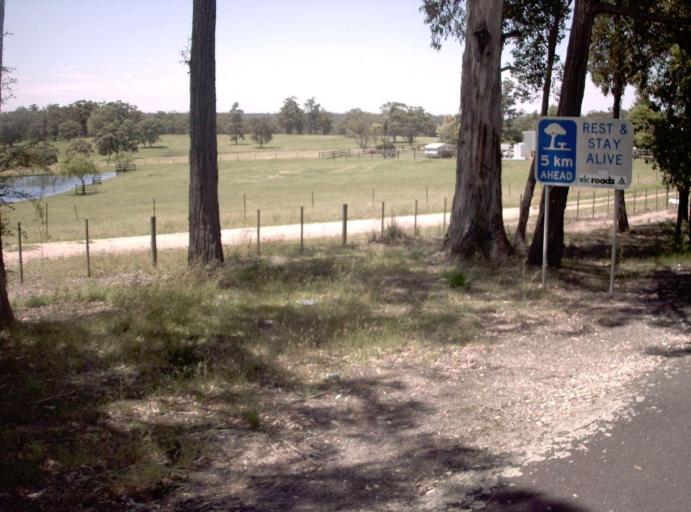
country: AU
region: Victoria
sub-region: East Gippsland
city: Lakes Entrance
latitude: -37.7326
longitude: 148.1426
